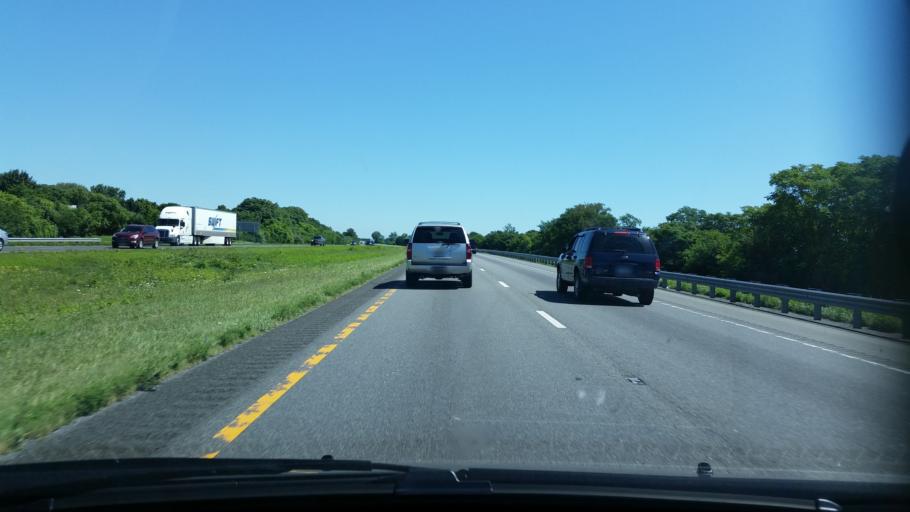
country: US
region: Virginia
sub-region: City of Winchester
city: Winchester
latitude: 39.2450
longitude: -78.1111
